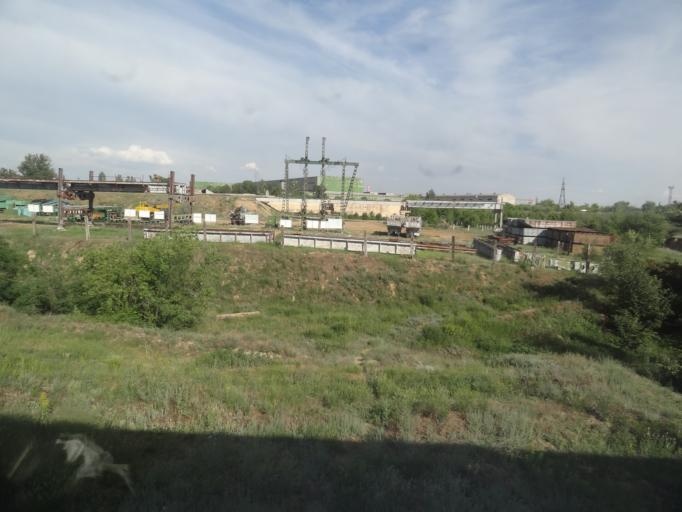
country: RU
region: Volgograd
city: Gumrak
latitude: 48.7634
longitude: 44.4352
